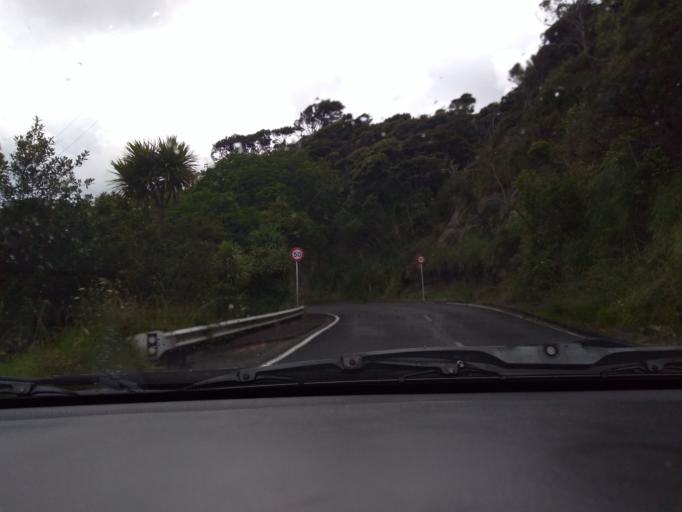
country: NZ
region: Auckland
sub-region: Auckland
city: Titirangi
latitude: -37.0045
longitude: 174.5791
